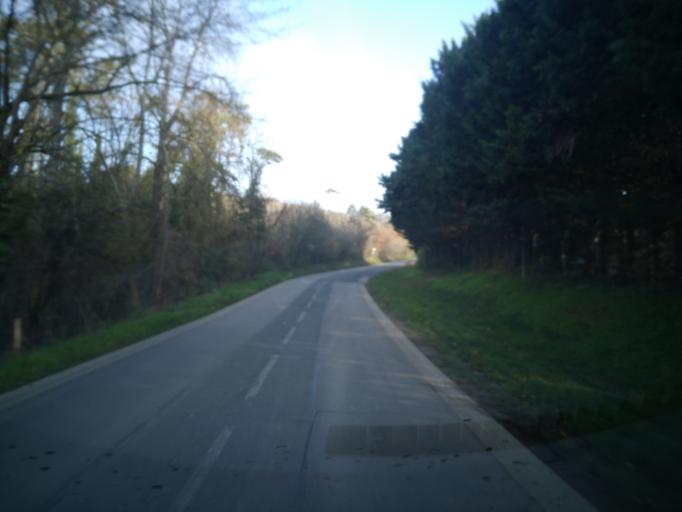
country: FR
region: Ile-de-France
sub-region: Departement des Yvelines
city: Saint-Germain-de-la-Grange
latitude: 48.8381
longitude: 1.9071
